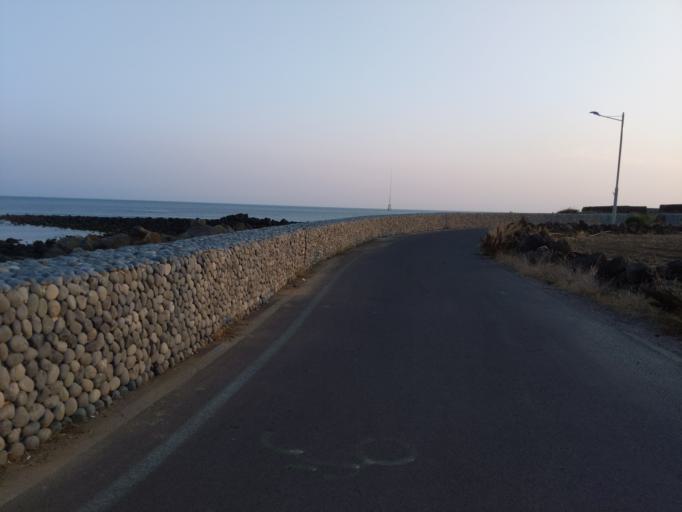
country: KR
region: Jeju-do
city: Gaigeturi
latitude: 33.2215
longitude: 126.2453
